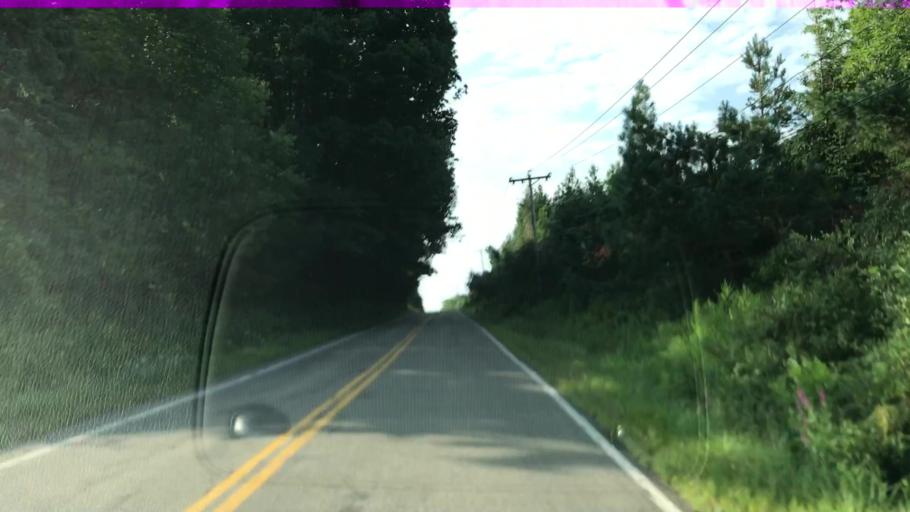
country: US
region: New York
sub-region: Chautauqua County
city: Mayville
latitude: 42.2613
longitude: -79.4699
